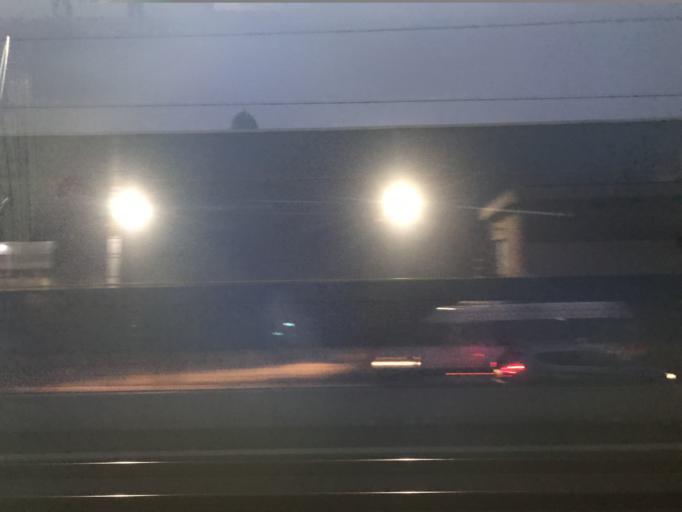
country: TR
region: Kocaeli
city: Darica
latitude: 40.8012
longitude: 29.3769
